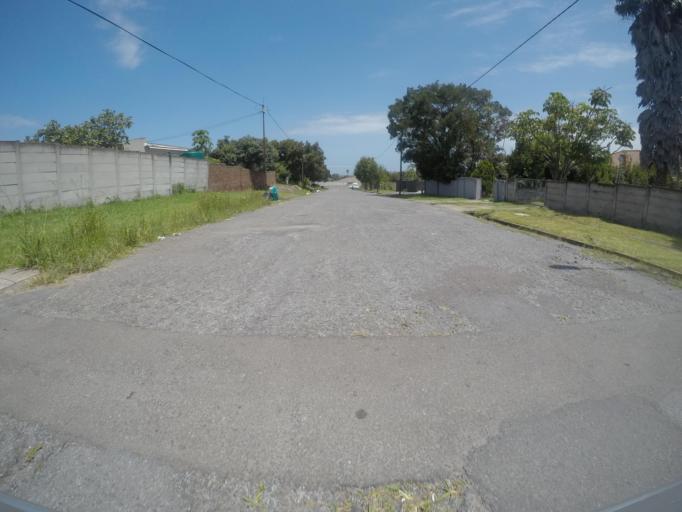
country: ZA
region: Eastern Cape
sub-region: Buffalo City Metropolitan Municipality
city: East London
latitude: -32.9747
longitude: 27.8831
